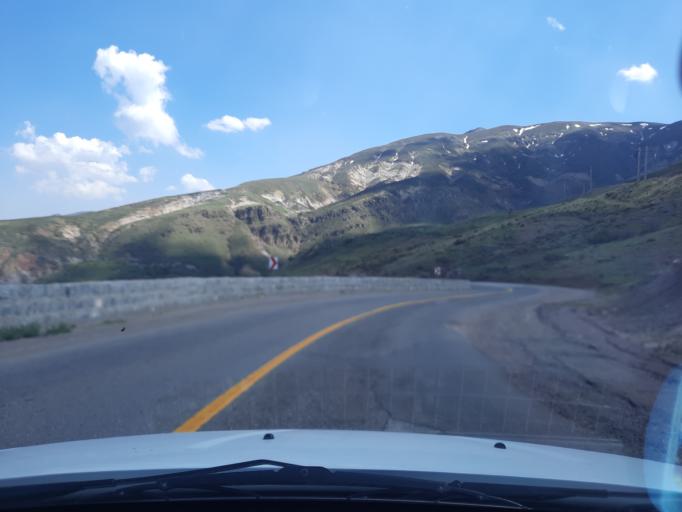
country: IR
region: Qazvin
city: Qazvin
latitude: 36.4070
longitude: 50.2217
